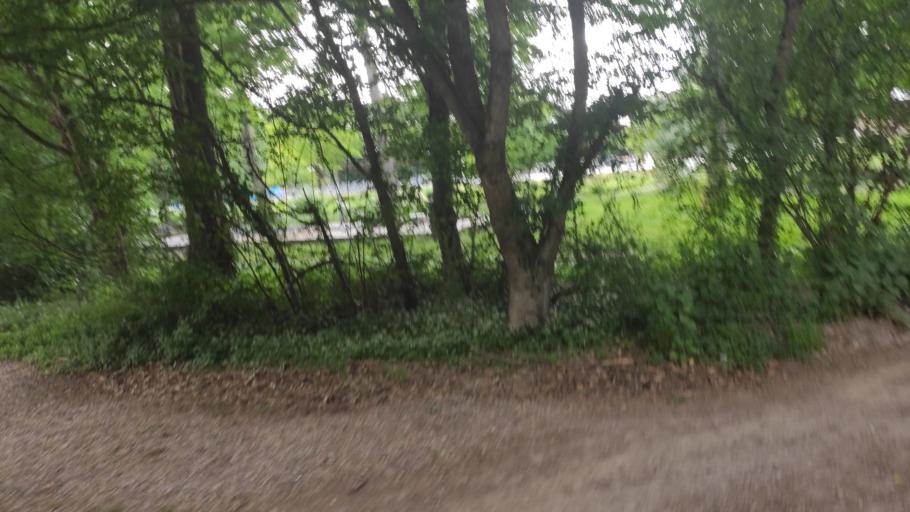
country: DE
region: Baden-Wuerttemberg
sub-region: Freiburg Region
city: Ebringen
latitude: 47.9823
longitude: 7.7685
